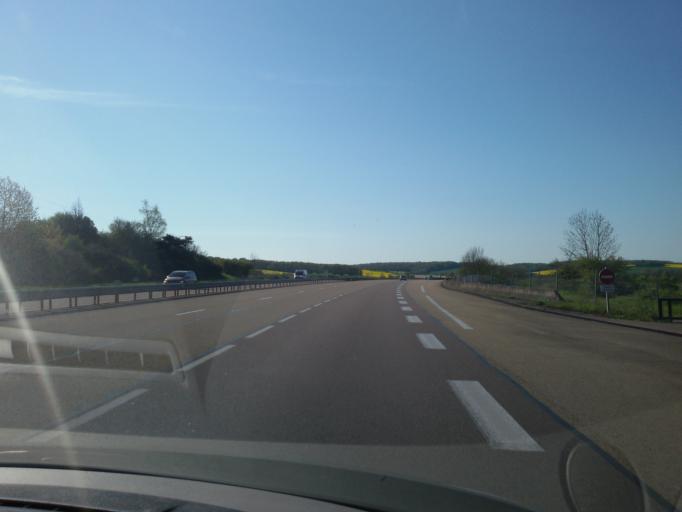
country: FR
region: Bourgogne
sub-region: Departement de l'Yonne
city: Saint-Julien-du-Sault
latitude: 47.9445
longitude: 3.2397
